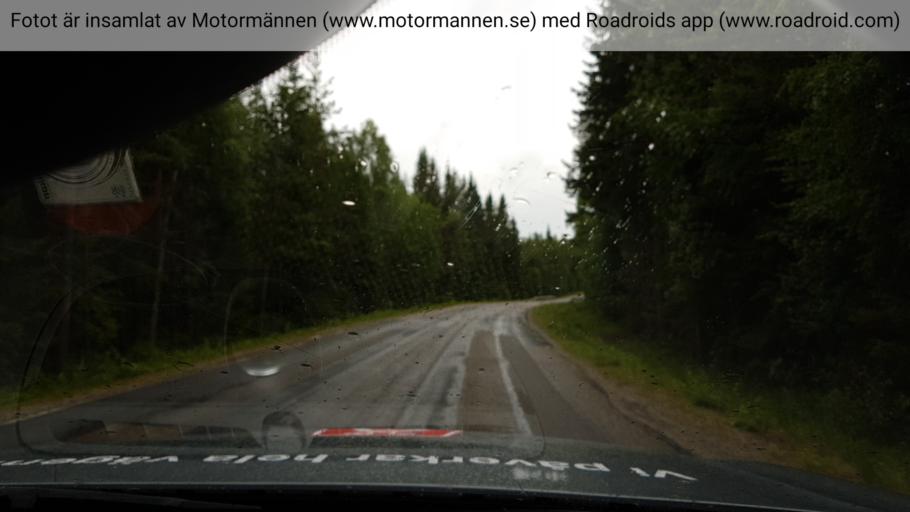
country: SE
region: Jaemtland
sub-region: Braecke Kommun
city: Braecke
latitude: 62.3865
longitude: 15.2290
